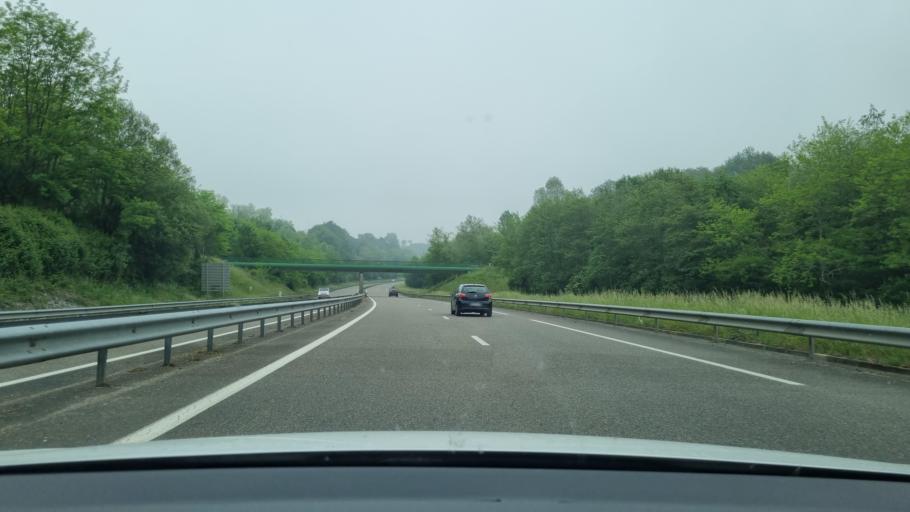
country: FR
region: Aquitaine
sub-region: Departement des Landes
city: Saint-Sever
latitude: 43.7515
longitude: -0.5556
